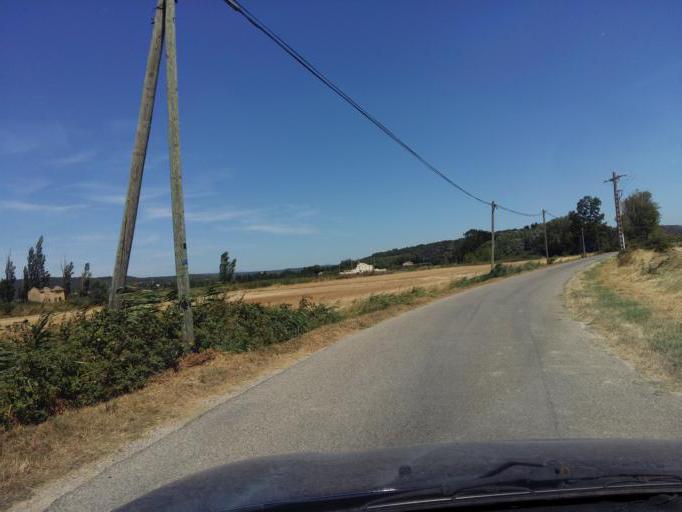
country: FR
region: Provence-Alpes-Cote d'Azur
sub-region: Departement du Vaucluse
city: Piolenc
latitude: 44.1684
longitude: 4.7439
